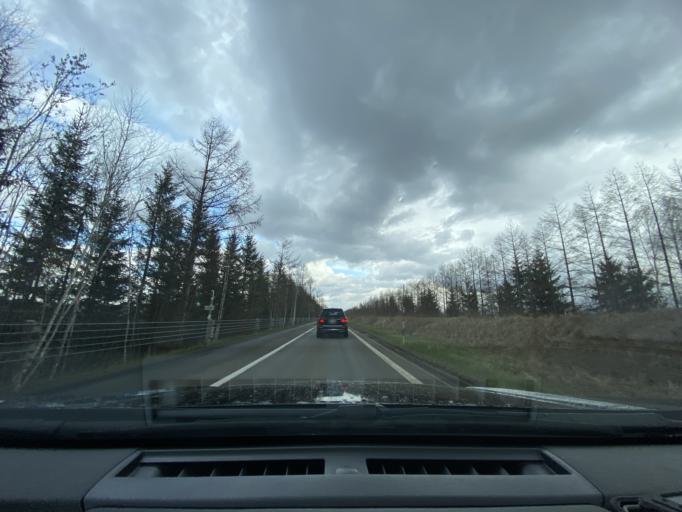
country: JP
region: Hokkaido
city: Otofuke
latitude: 42.9807
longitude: 142.9685
